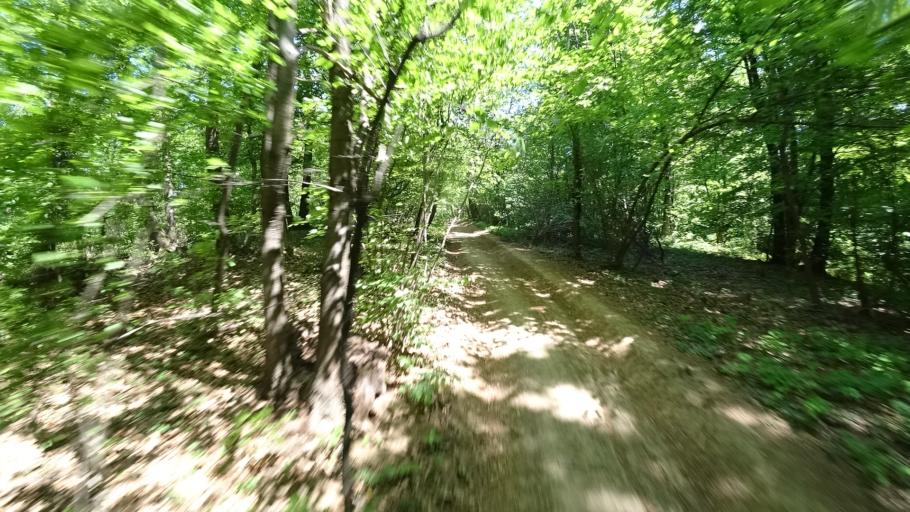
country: HR
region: Zagrebacka
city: Jablanovec
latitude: 45.8402
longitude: 15.8432
